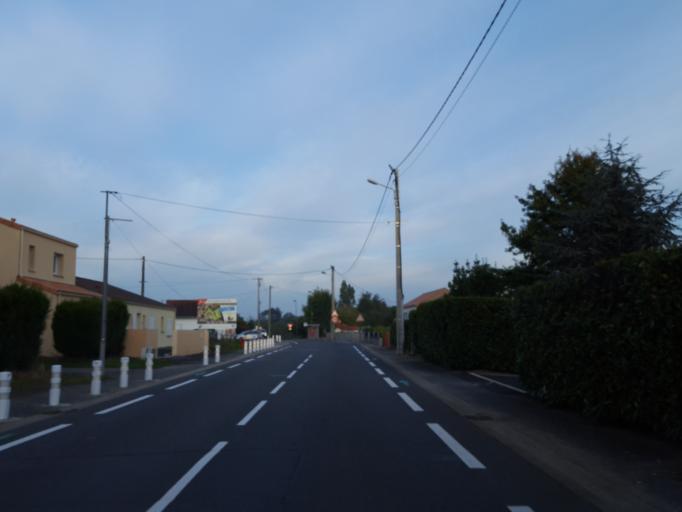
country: FR
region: Pays de la Loire
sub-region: Departement de la Loire-Atlantique
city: Haute-Goulaine
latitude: 47.2002
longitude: -1.4423
